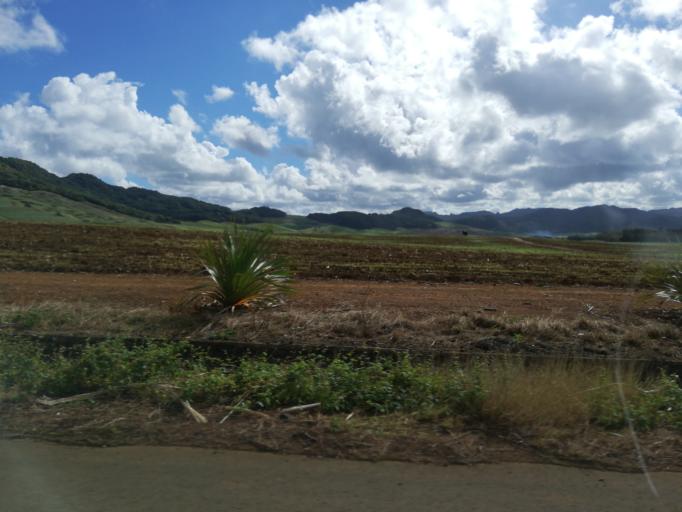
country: MU
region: Grand Port
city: Mahebourg
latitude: -20.3755
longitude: 57.6995
